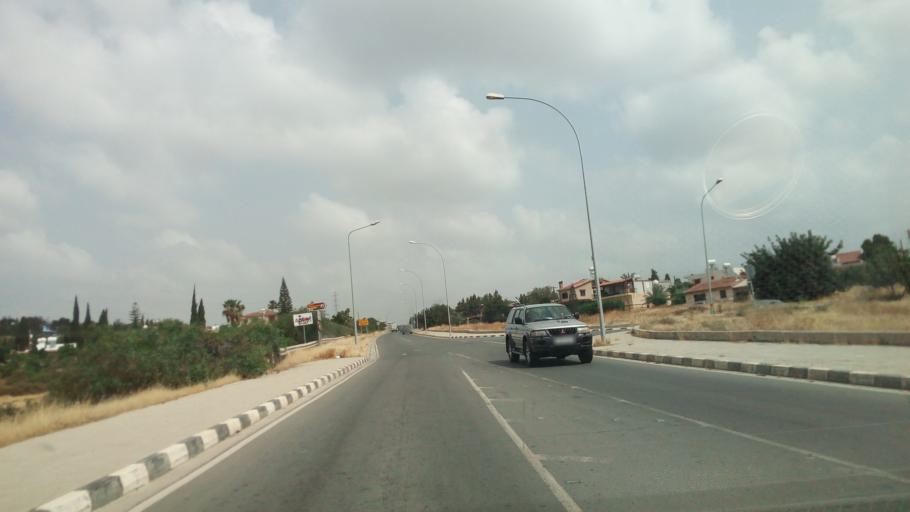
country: CY
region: Limassol
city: Pano Polemidia
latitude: 34.6964
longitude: 32.9875
